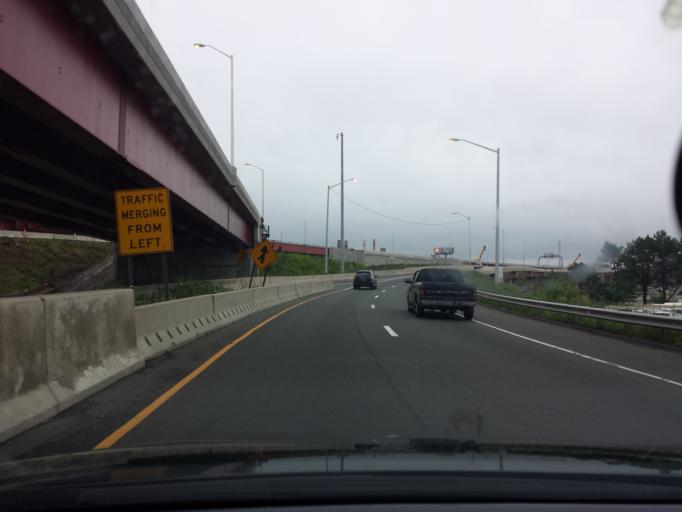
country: US
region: Connecticut
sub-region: New Haven County
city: New Haven
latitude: 41.2996
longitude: -72.9144
